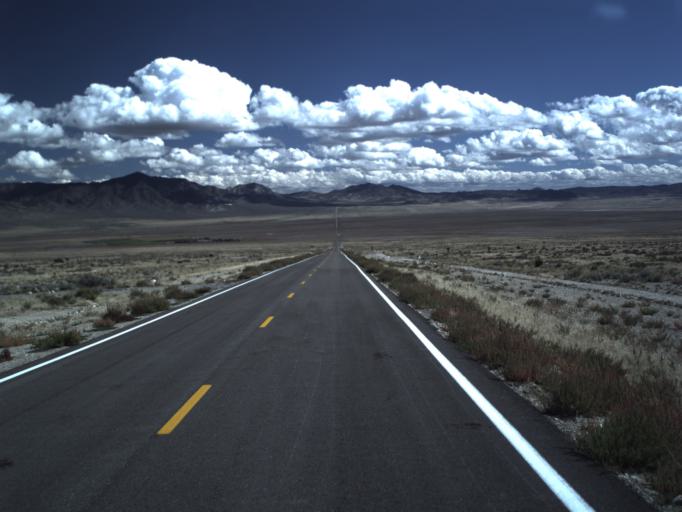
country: US
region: Utah
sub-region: Beaver County
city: Milford
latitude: 38.4994
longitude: -113.4959
